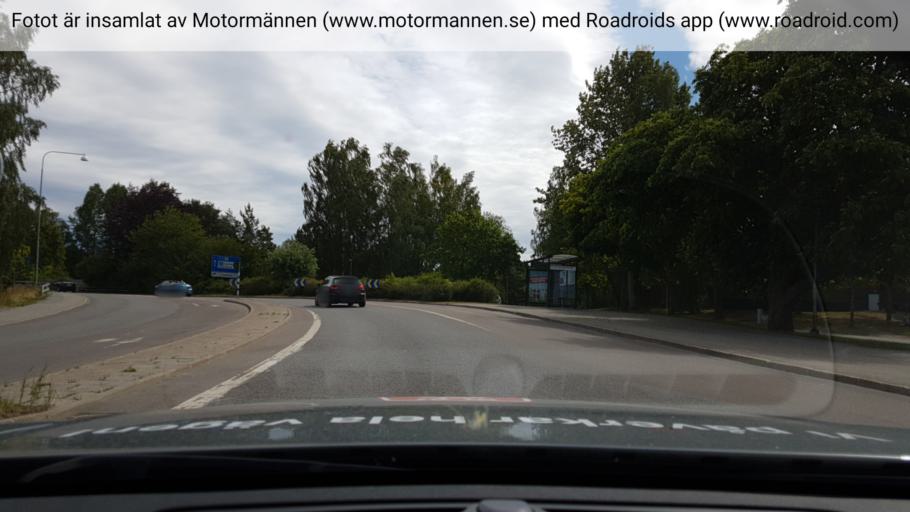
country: SE
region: Stockholm
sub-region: Nynashamns Kommun
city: Nynashamn
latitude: 58.9161
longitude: 17.9409
